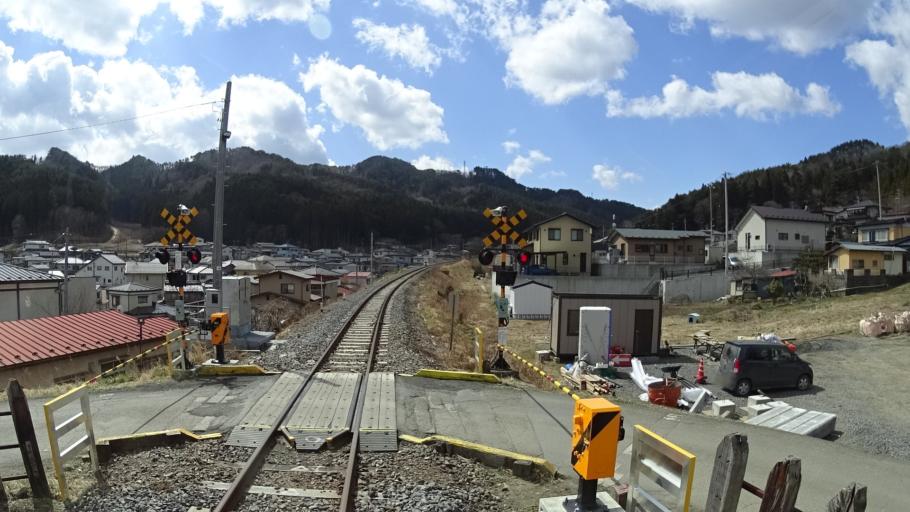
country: JP
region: Iwate
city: Otsuchi
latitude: 39.3691
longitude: 141.9382
